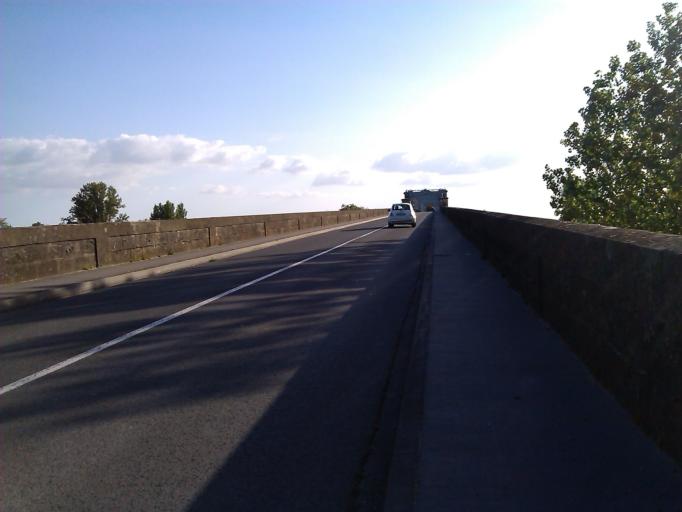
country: FR
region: Aquitaine
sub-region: Departement de la Gironde
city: Cubzac-les-Ponts
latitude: 44.9642
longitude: -0.4566
